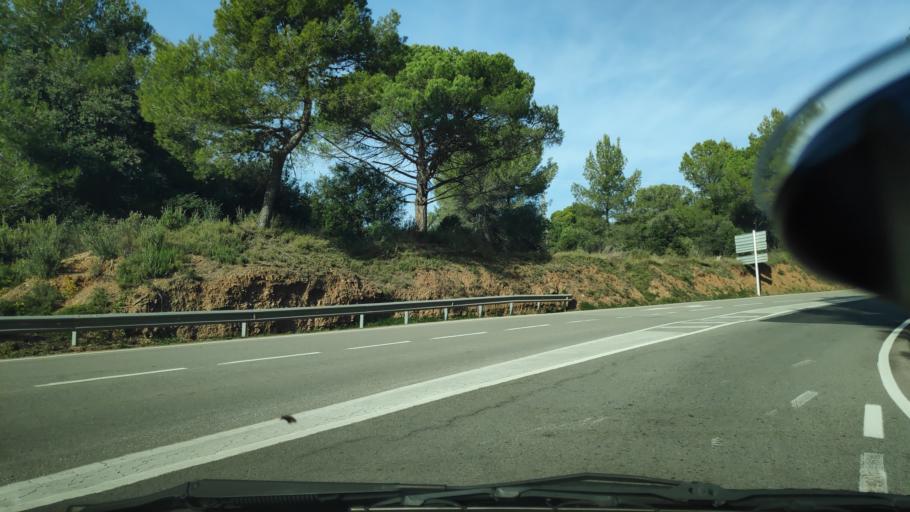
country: ES
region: Catalonia
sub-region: Provincia de Barcelona
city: Matadepera
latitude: 41.5945
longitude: 2.0379
